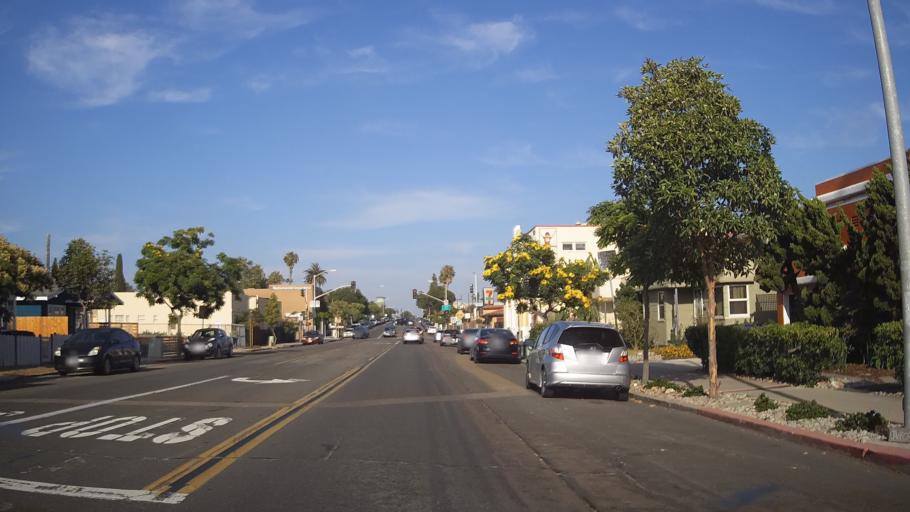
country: US
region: California
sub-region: San Diego County
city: San Diego
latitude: 32.7573
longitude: -117.1314
